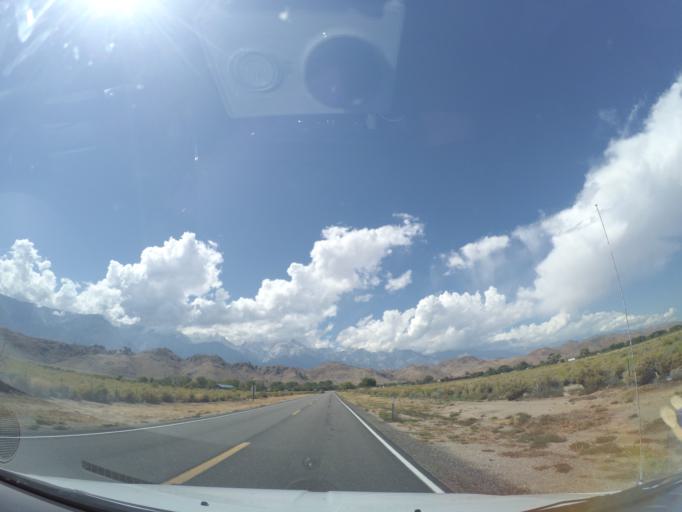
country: US
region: California
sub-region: Inyo County
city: Lone Pine
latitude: 36.5793
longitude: -118.0512
